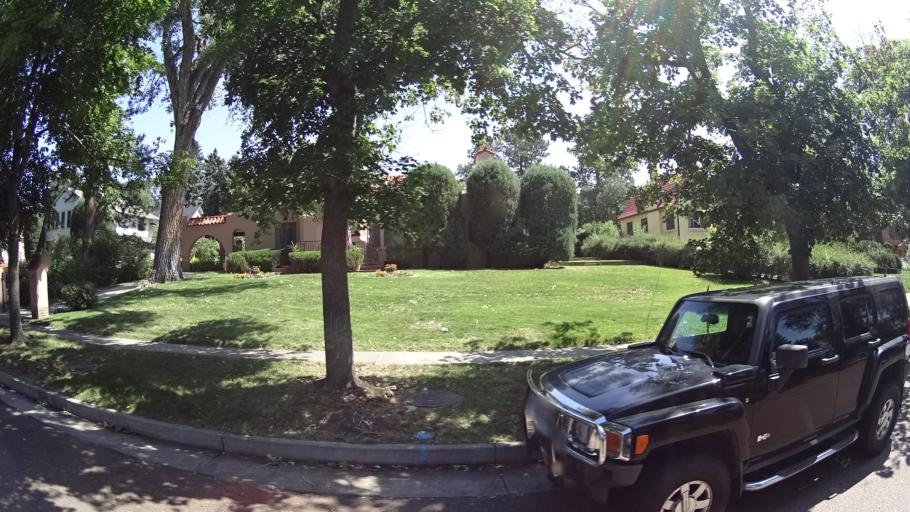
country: US
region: Colorado
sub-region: El Paso County
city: Colorado Springs
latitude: 38.8554
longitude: -104.8275
